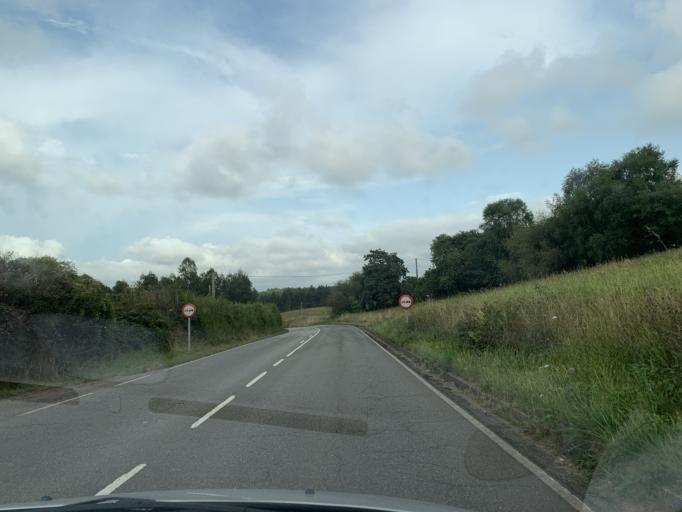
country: ES
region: Asturias
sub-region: Province of Asturias
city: Villaviciosa
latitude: 43.5169
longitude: -5.4317
